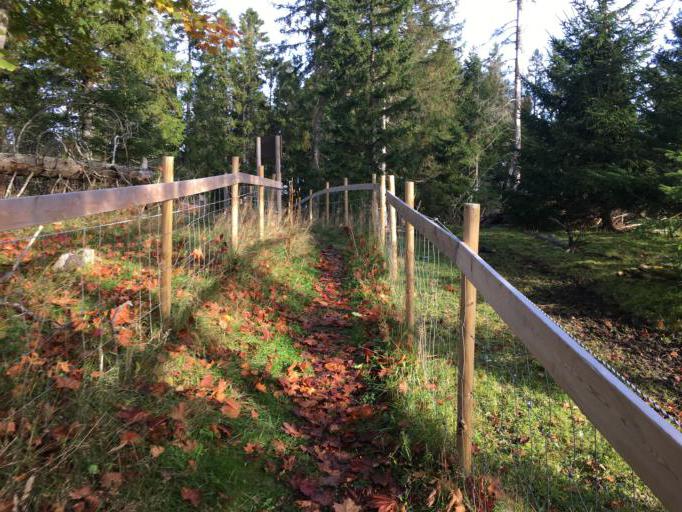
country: NO
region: Nord-Trondelag
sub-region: Leksvik
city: Leksvik
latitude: 63.5727
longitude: 10.6128
